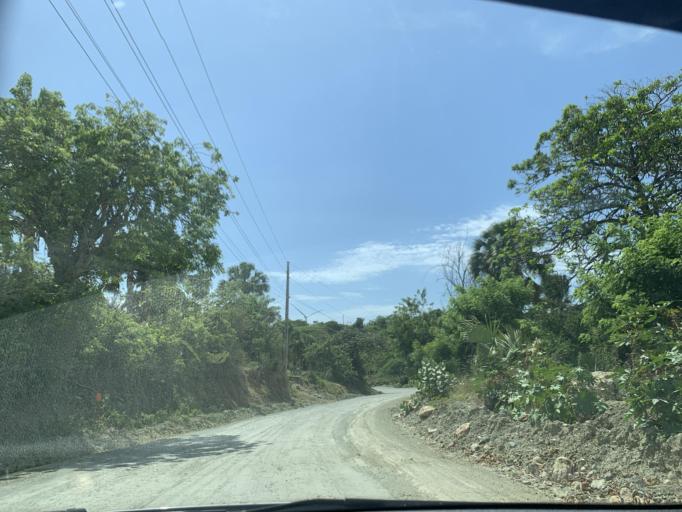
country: DO
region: Puerto Plata
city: Imbert
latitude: 19.8675
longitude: -70.8187
